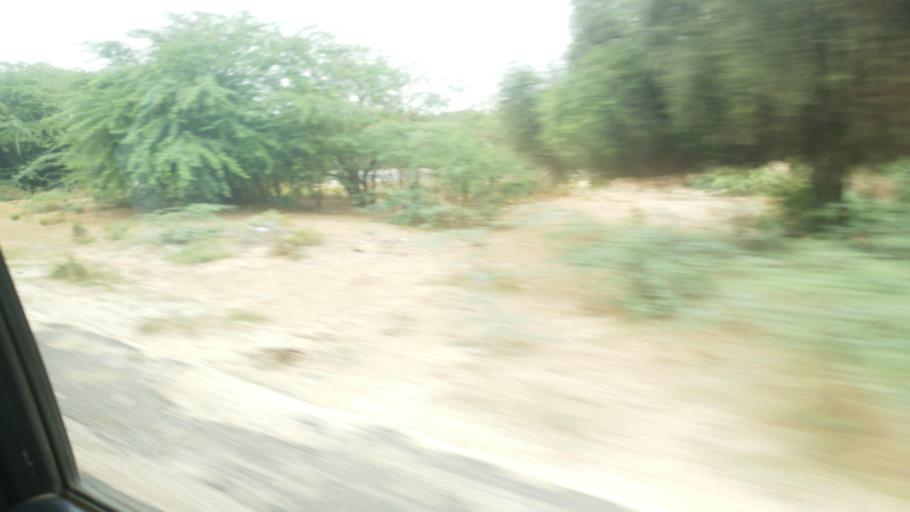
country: SN
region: Saint-Louis
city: Saint-Louis
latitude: 16.0749
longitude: -16.3842
